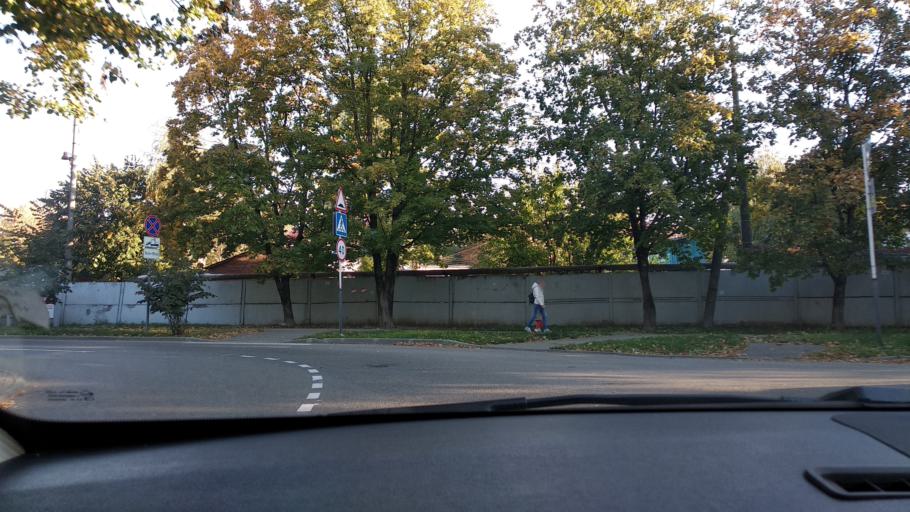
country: RU
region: Adygeya
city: Yablonovskiy
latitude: 45.0092
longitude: 38.9648
